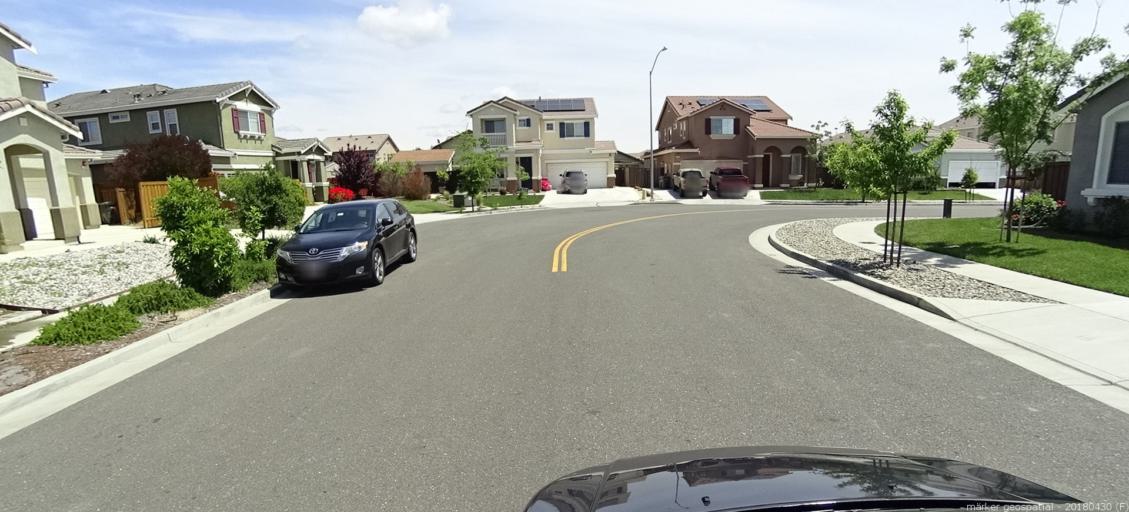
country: US
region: California
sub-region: Yolo County
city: West Sacramento
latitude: 38.5508
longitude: -121.5223
